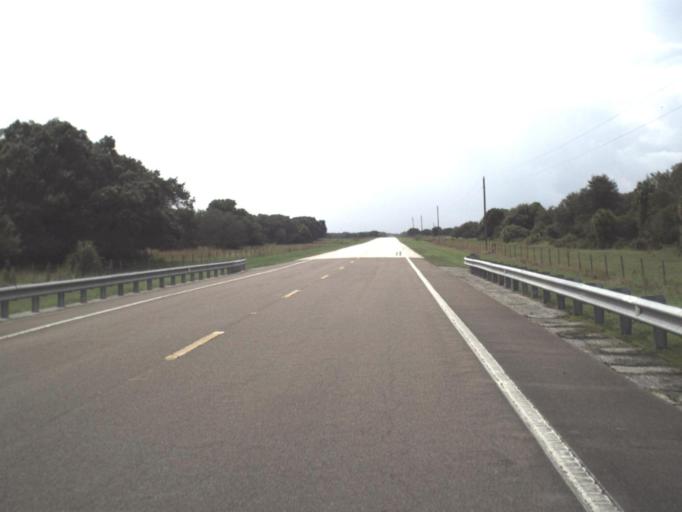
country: US
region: Florida
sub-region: Sarasota County
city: North Port
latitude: 27.1934
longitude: -82.1559
